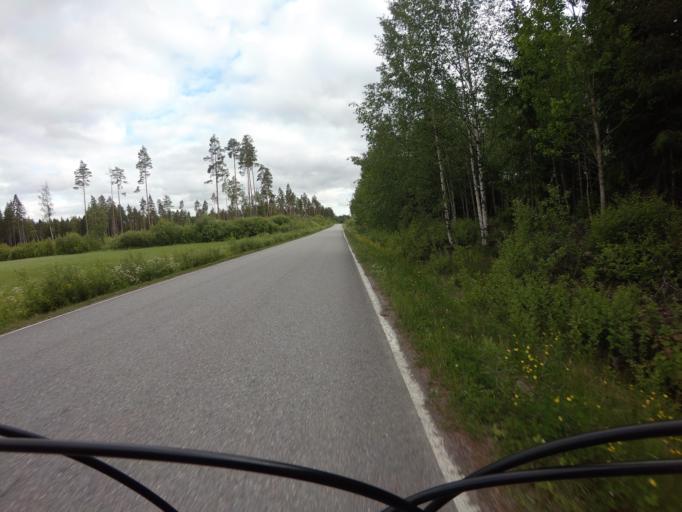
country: FI
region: Varsinais-Suomi
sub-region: Turku
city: Lieto
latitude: 60.5173
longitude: 22.3831
